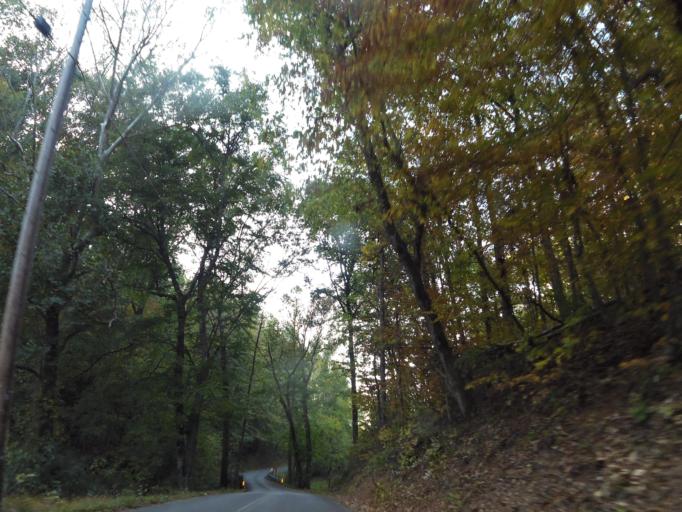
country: US
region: Tennessee
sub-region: Blount County
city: Eagleton Village
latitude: 35.8665
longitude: -83.9175
